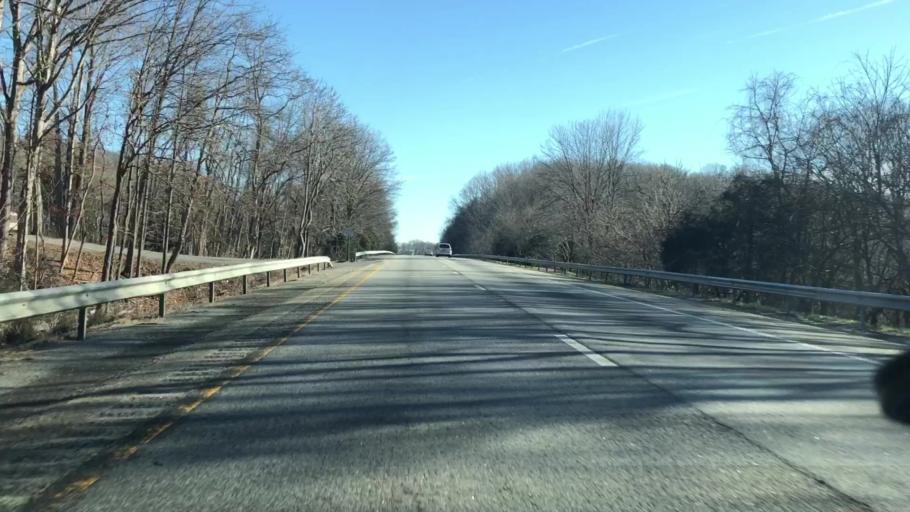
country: US
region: Virginia
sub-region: Botetourt County
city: Buchanan
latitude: 37.6109
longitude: -79.6044
